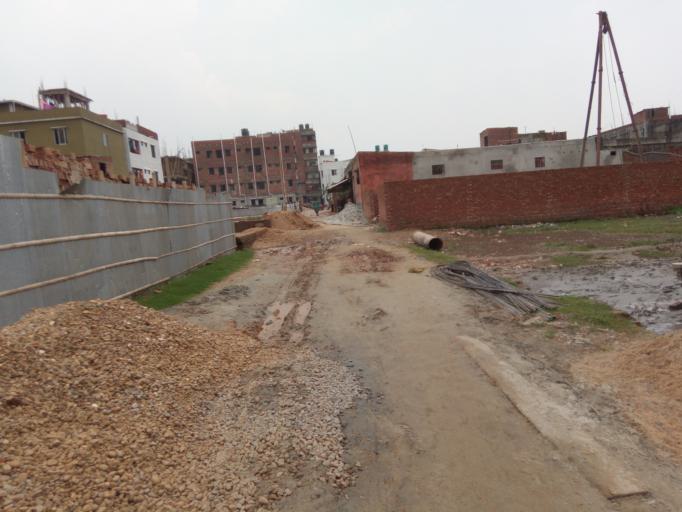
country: BD
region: Dhaka
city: Azimpur
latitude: 23.7563
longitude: 90.3519
